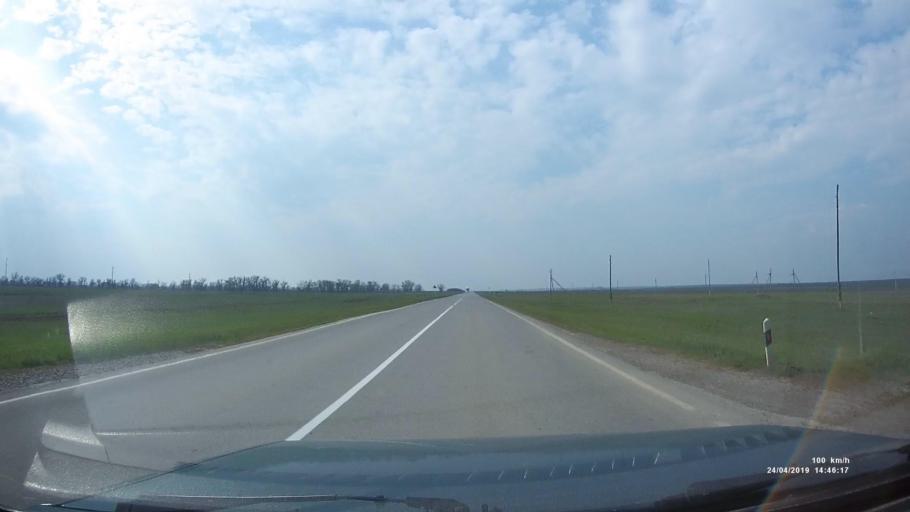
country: RU
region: Rostov
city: Remontnoye
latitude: 46.4804
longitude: 43.7929
